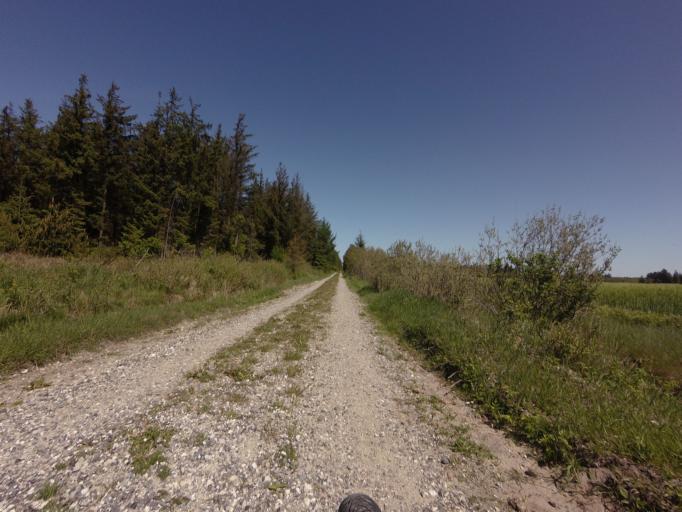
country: DK
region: North Denmark
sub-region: Jammerbugt Kommune
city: Kas
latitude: 57.2245
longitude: 9.5791
